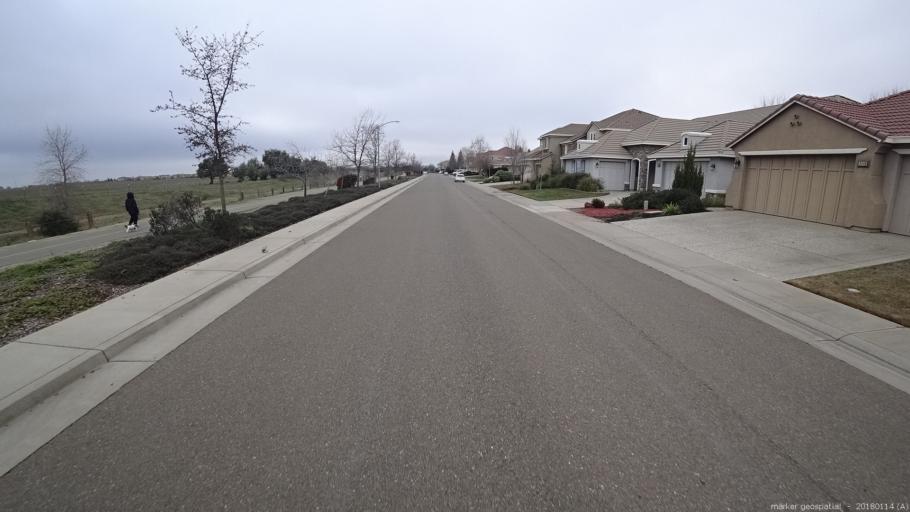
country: US
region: California
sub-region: Sacramento County
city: Gold River
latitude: 38.5429
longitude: -121.2282
